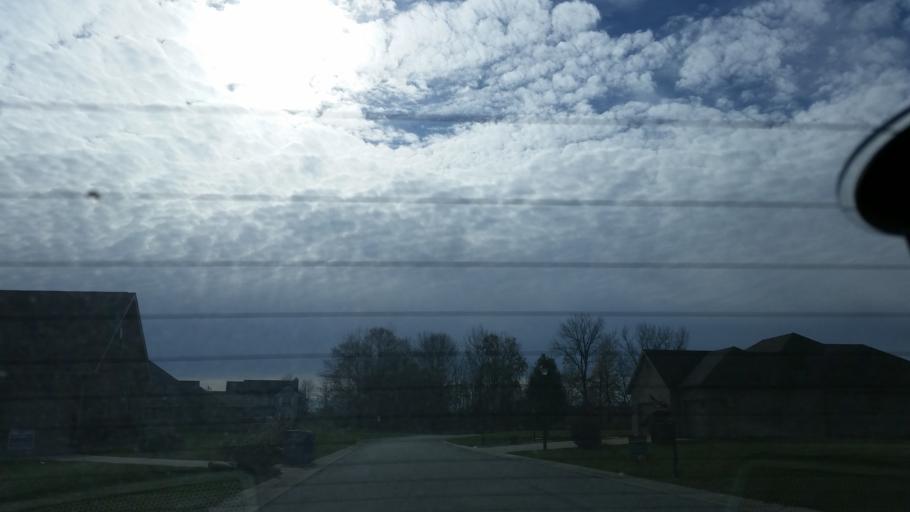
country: US
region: Indiana
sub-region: Howard County
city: Indian Heights
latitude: 40.4277
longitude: -86.1560
